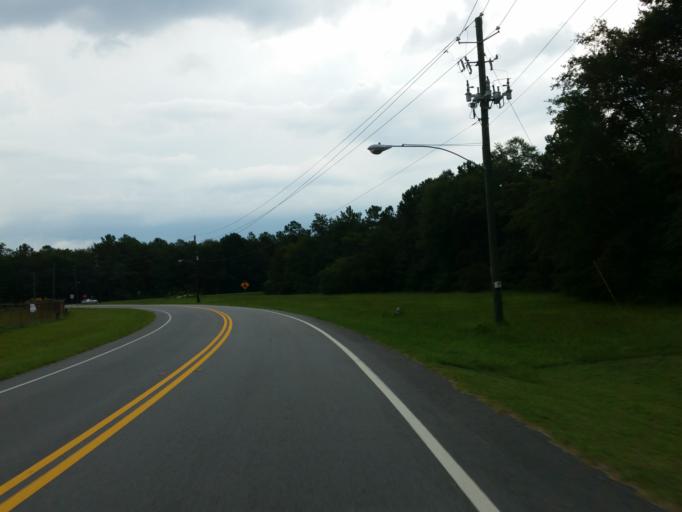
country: US
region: Georgia
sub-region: Tift County
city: Unionville
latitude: 31.4135
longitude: -83.4823
